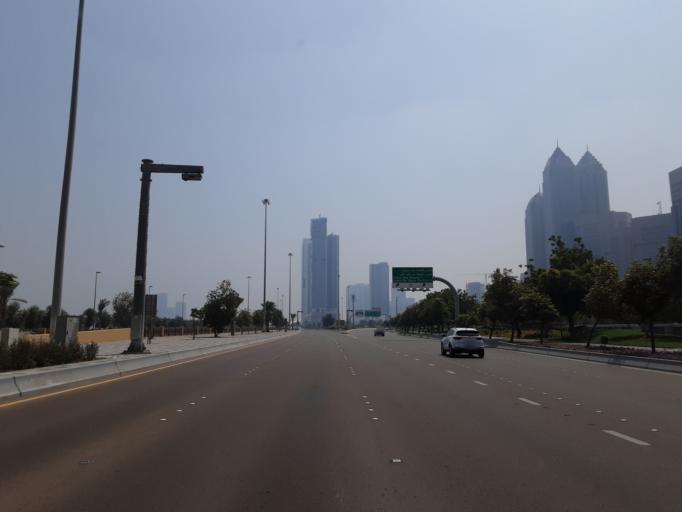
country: AE
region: Abu Dhabi
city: Abu Dhabi
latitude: 24.4970
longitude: 54.3610
